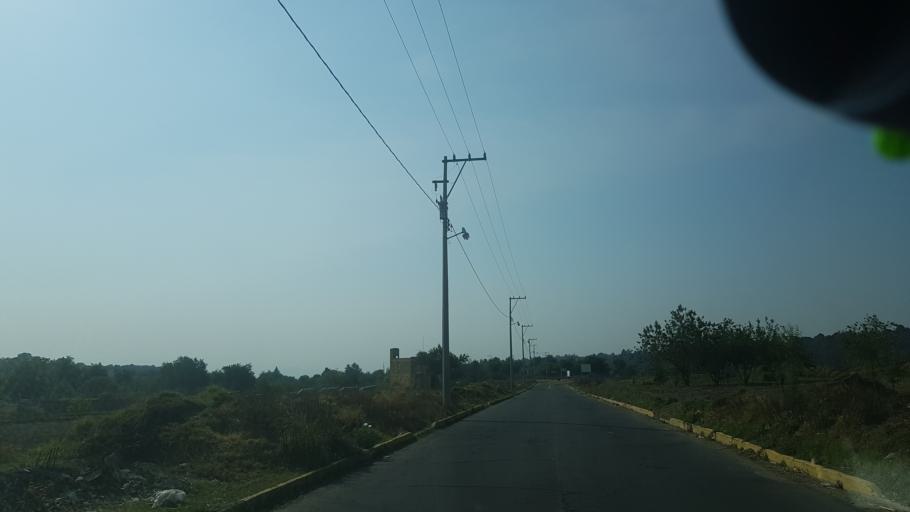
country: MX
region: Puebla
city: San Nicolas de los Ranchos
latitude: 19.0649
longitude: -98.4727
